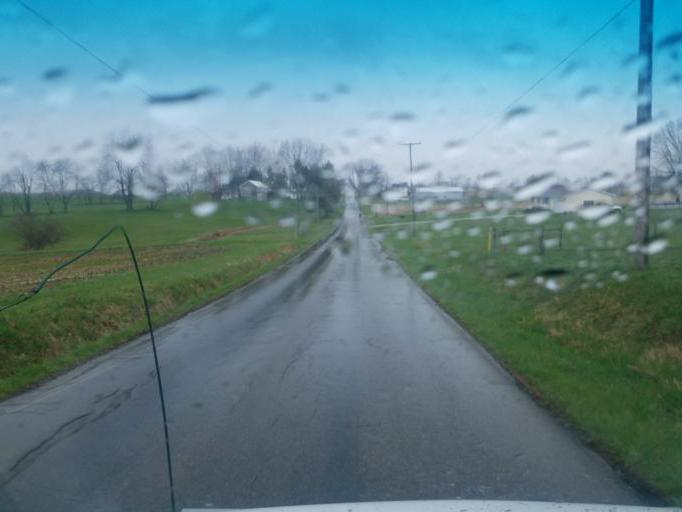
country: US
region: Ohio
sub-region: Wayne County
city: Apple Creek
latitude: 40.7170
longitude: -81.9153
